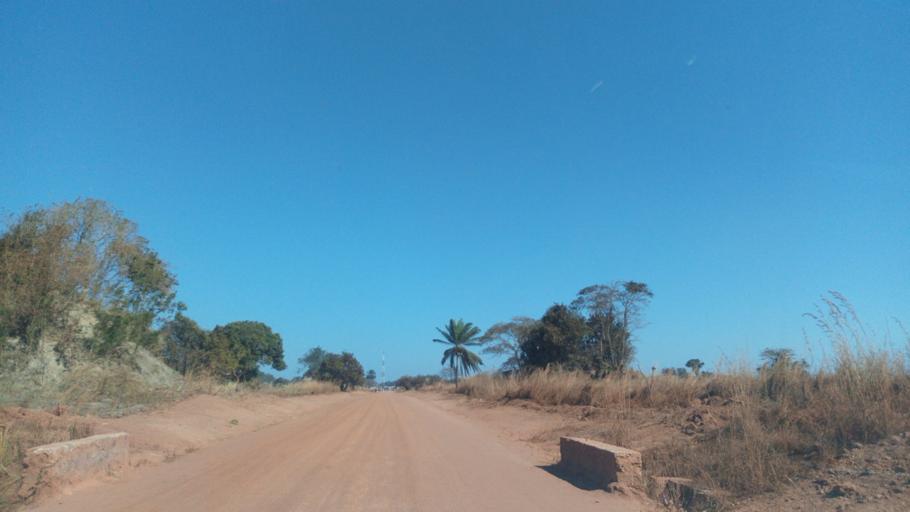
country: ZM
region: Luapula
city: Mwense
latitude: -10.7560
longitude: 28.2914
